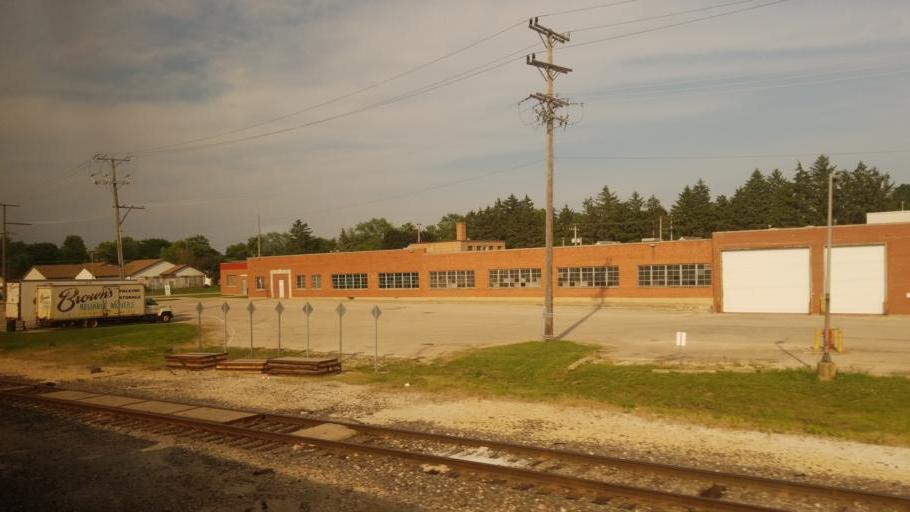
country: US
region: Illinois
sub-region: Kane County
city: Montgomery
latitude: 41.7247
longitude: -88.3489
